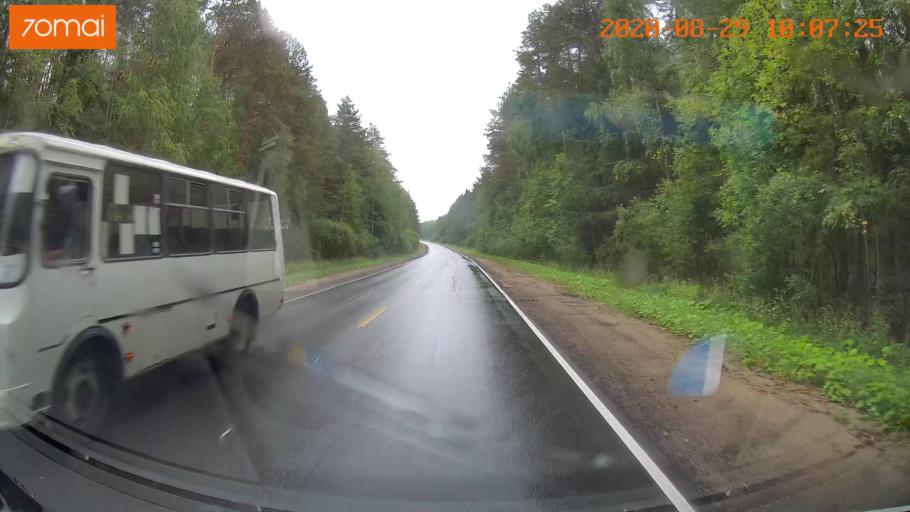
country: RU
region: Ivanovo
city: Kuznechikha
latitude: 57.3809
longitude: 42.5666
